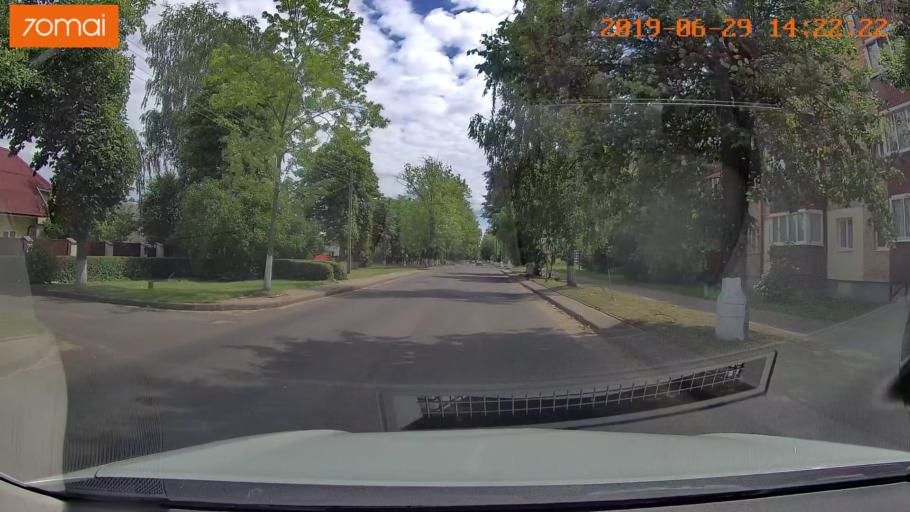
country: BY
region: Minsk
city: Salihorsk
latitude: 52.7920
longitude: 27.5498
